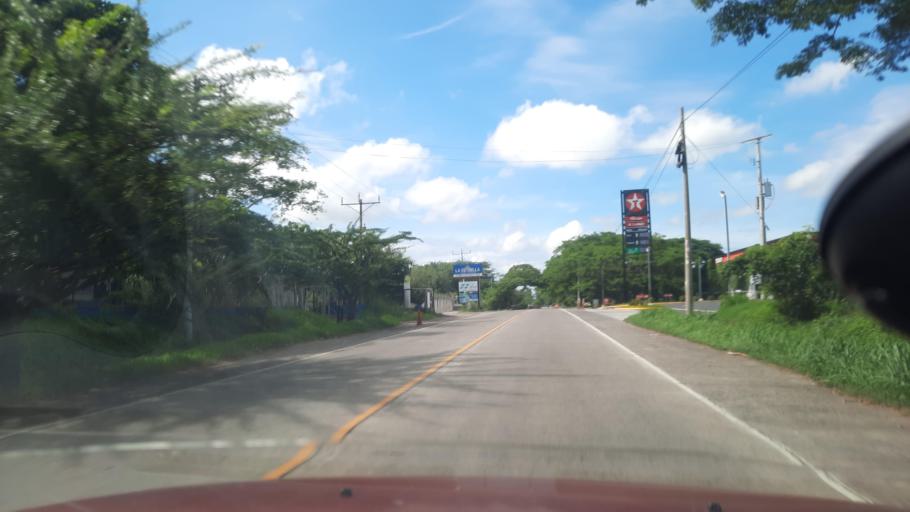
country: SV
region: Usulutan
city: San Agustin
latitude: 13.4400
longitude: -88.7078
